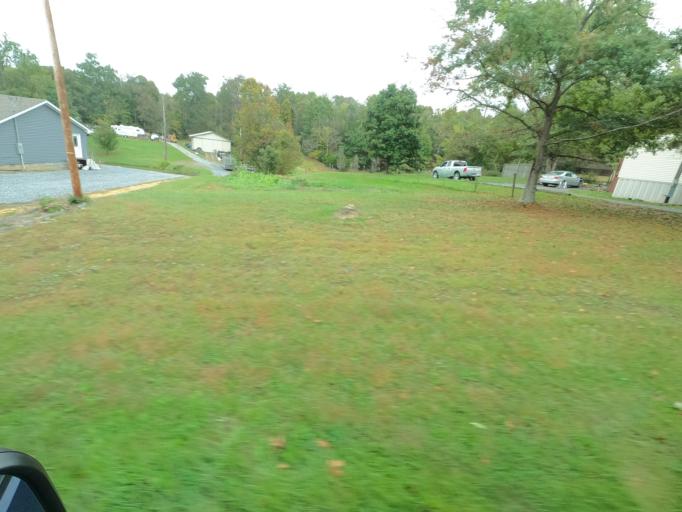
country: US
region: Tennessee
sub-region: Washington County
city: Jonesborough
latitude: 36.2482
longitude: -82.5897
